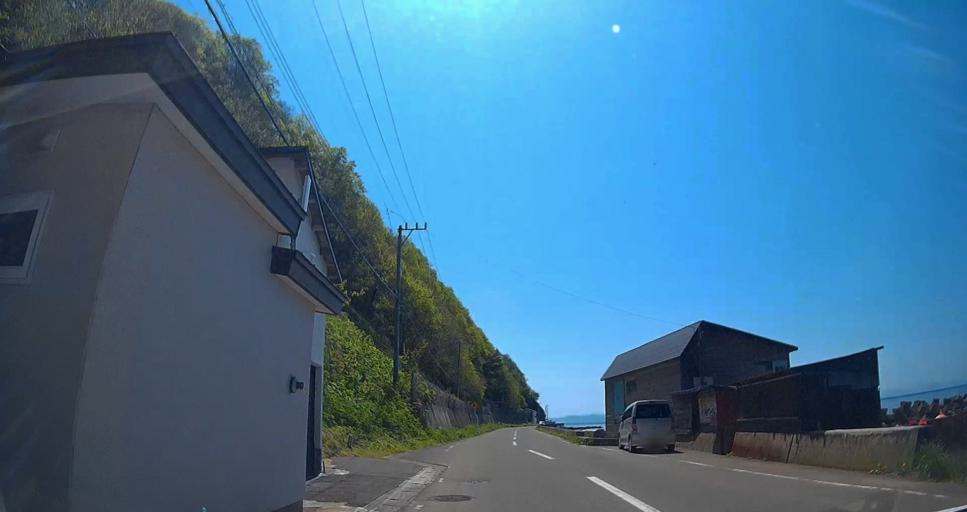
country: JP
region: Aomori
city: Aomori Shi
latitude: 41.1324
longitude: 140.7945
